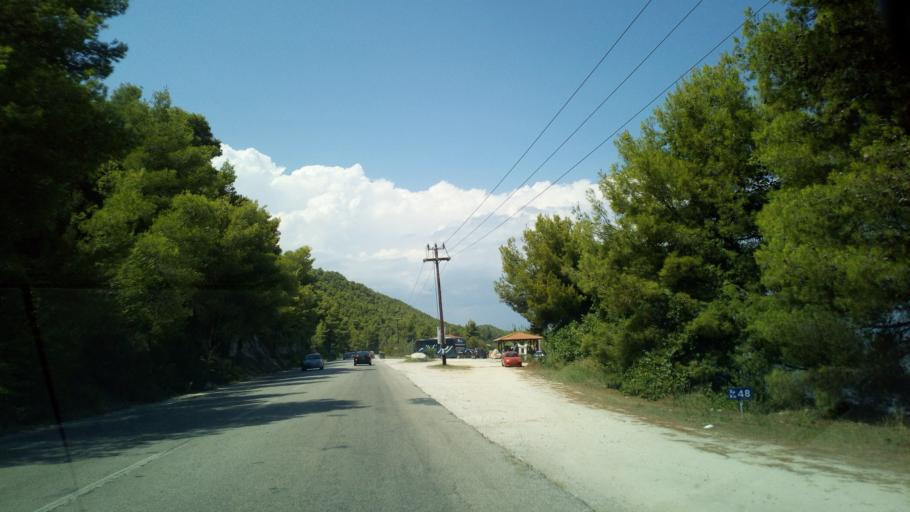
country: GR
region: Central Macedonia
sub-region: Nomos Chalkidikis
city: Agios Nikolaos
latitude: 40.1995
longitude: 23.7654
